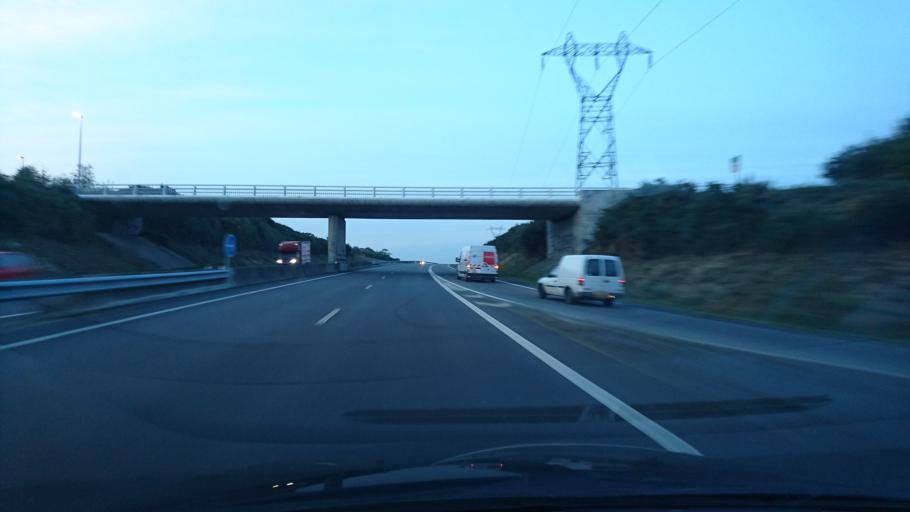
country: FR
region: Brittany
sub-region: Departement d'Ille-et-Vilaine
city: Guichen
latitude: 47.9900
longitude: -1.8138
